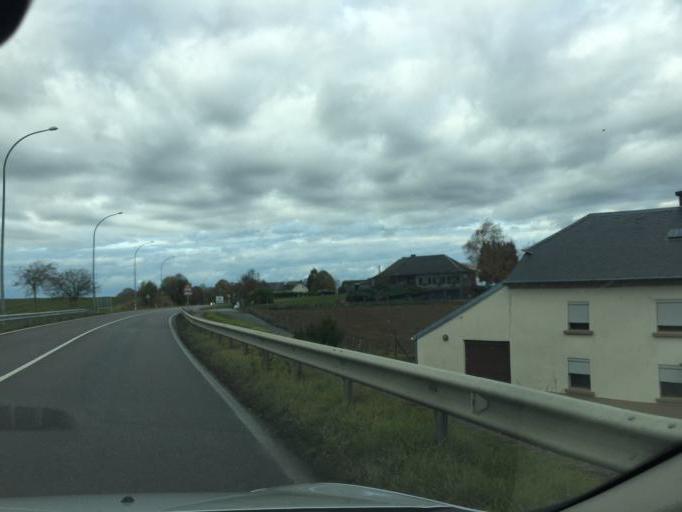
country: LU
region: Diekirch
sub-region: Canton de Wiltz
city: Goesdorf
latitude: 49.8870
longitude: 5.9710
